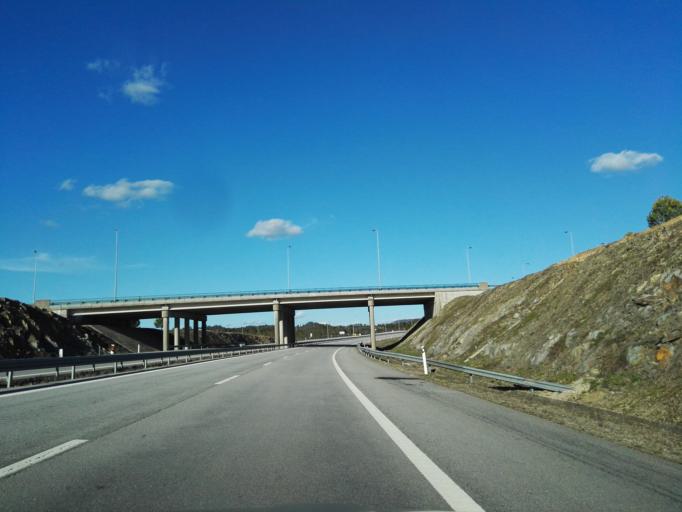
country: PT
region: Portalegre
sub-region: Nisa
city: Nisa
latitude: 39.6290
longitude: -7.7545
